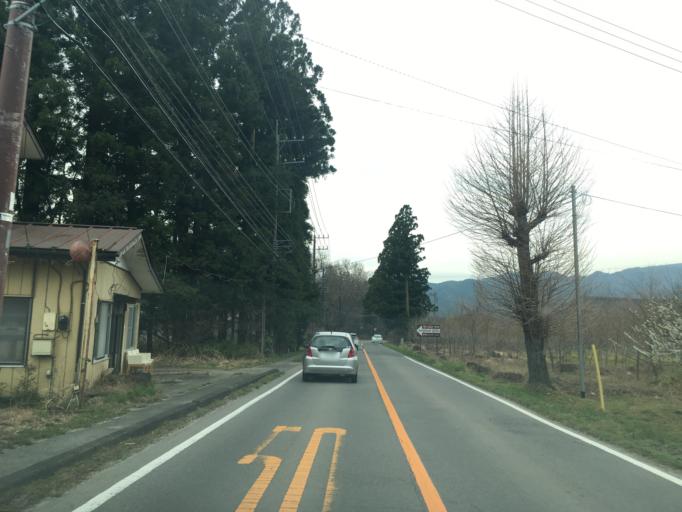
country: JP
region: Tochigi
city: Kuroiso
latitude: 36.9561
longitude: 139.9035
